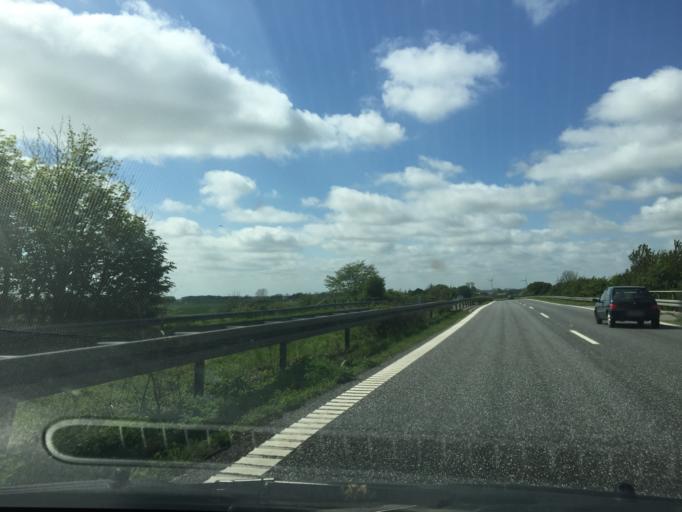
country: DK
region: Zealand
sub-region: Lolland Kommune
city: Maribo
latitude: 54.7899
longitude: 11.5617
